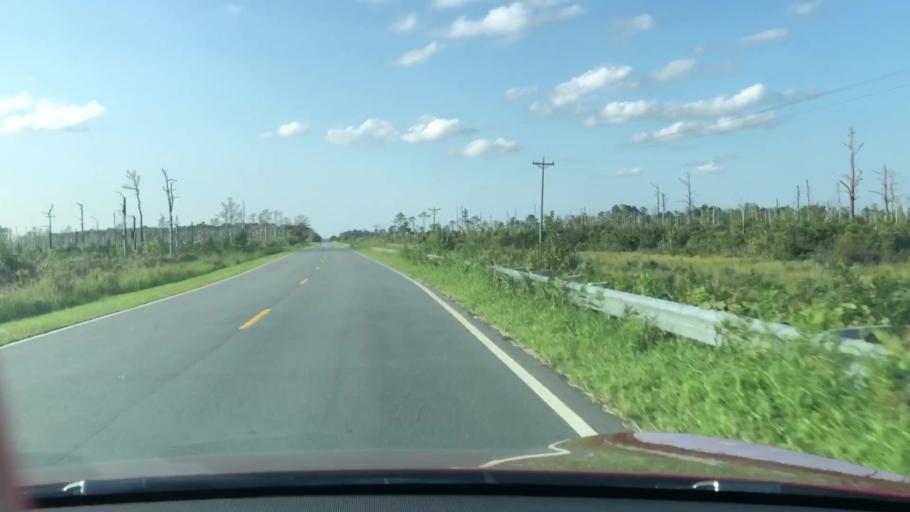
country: US
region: North Carolina
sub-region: Dare County
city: Wanchese
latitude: 35.6596
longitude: -75.7773
